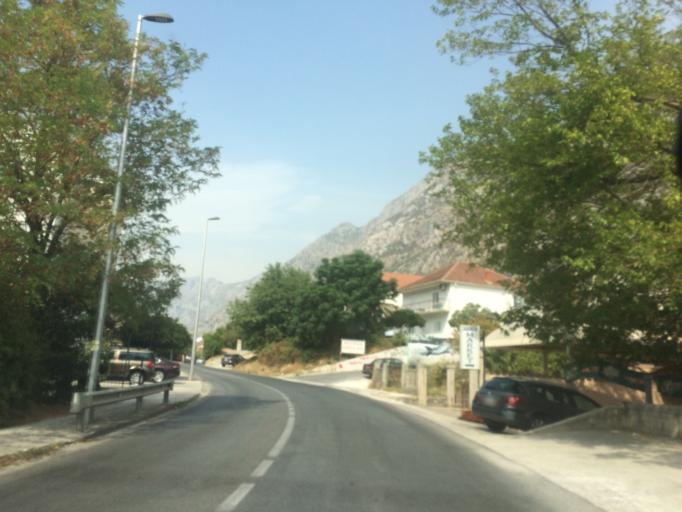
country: ME
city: Dobrota
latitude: 42.4440
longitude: 18.7657
